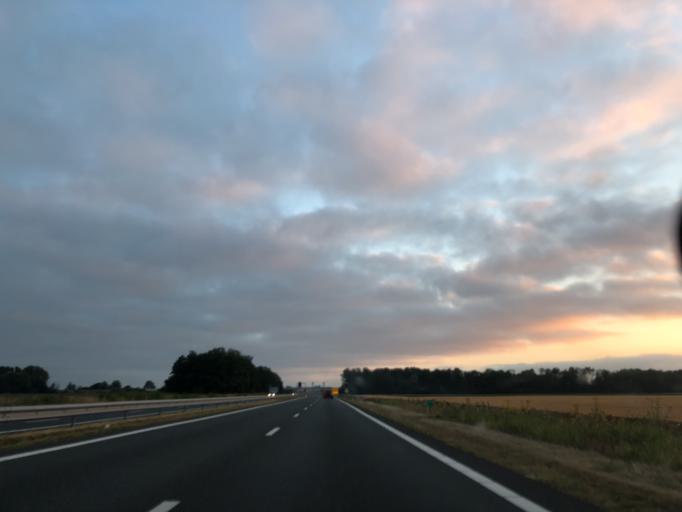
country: NL
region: Groningen
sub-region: Gemeente Veendam
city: Veendam
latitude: 53.1561
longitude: 6.8962
